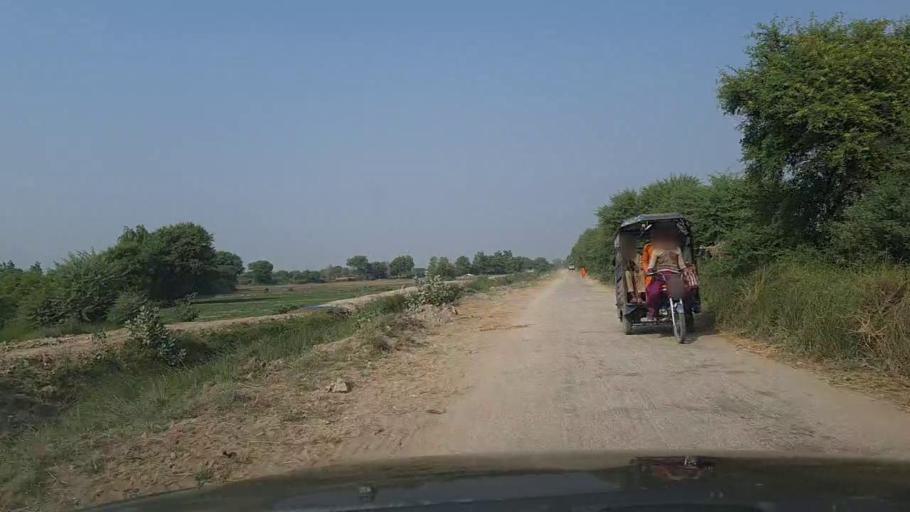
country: PK
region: Sindh
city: Mirpur Batoro
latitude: 24.7185
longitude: 68.2552
